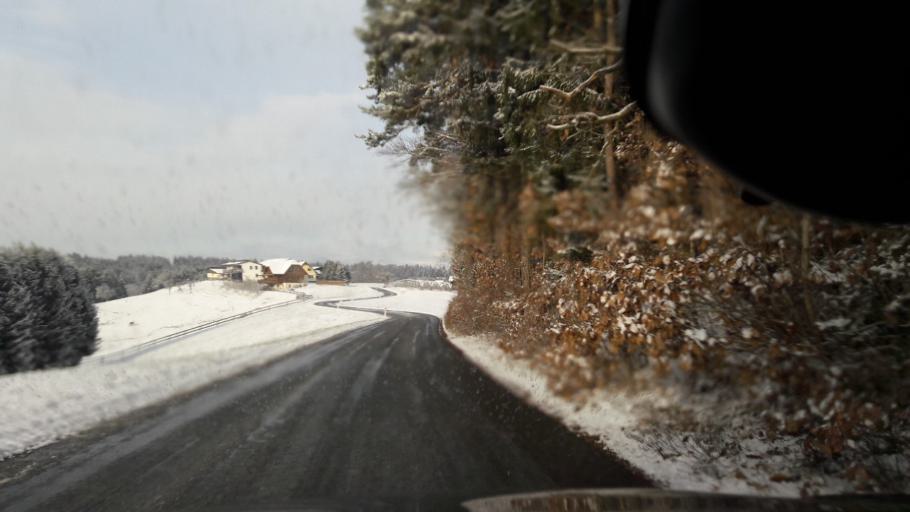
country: AT
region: Styria
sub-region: Politischer Bezirk Graz-Umgebung
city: Sankt Oswald bei Plankenwarth
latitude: 47.0927
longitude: 15.2554
